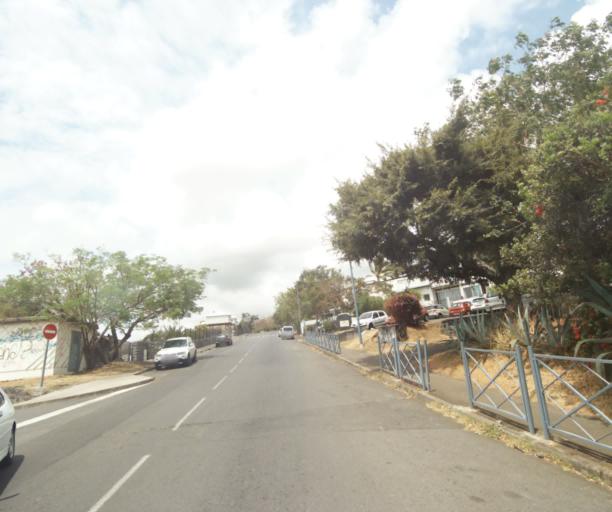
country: RE
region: Reunion
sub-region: Reunion
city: Saint-Paul
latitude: -21.0214
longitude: 55.2664
